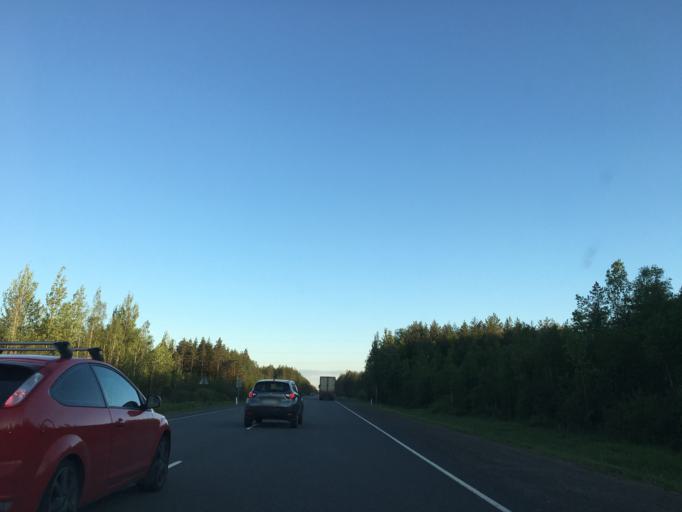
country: RU
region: Leningrad
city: Rozhdestveno
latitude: 59.2989
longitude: 29.9412
